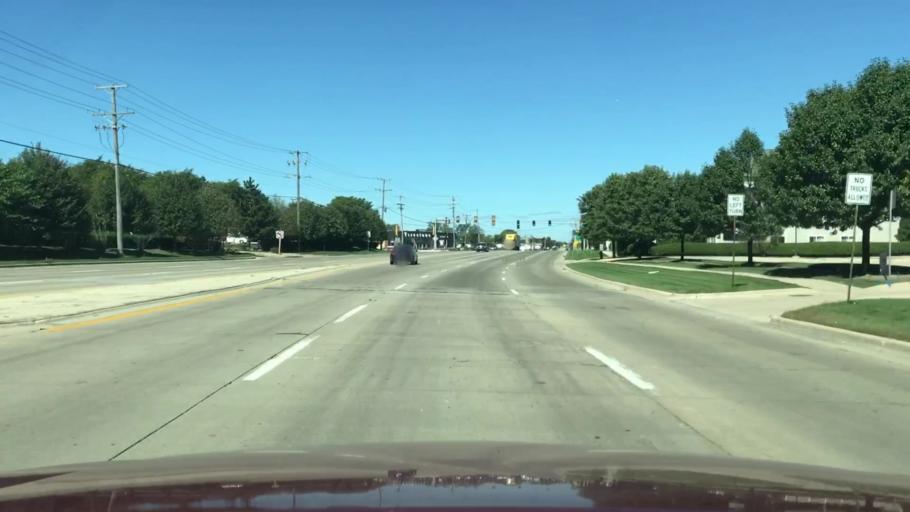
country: US
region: Illinois
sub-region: Cook County
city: Elk Grove Village
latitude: 42.0093
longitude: -87.9428
